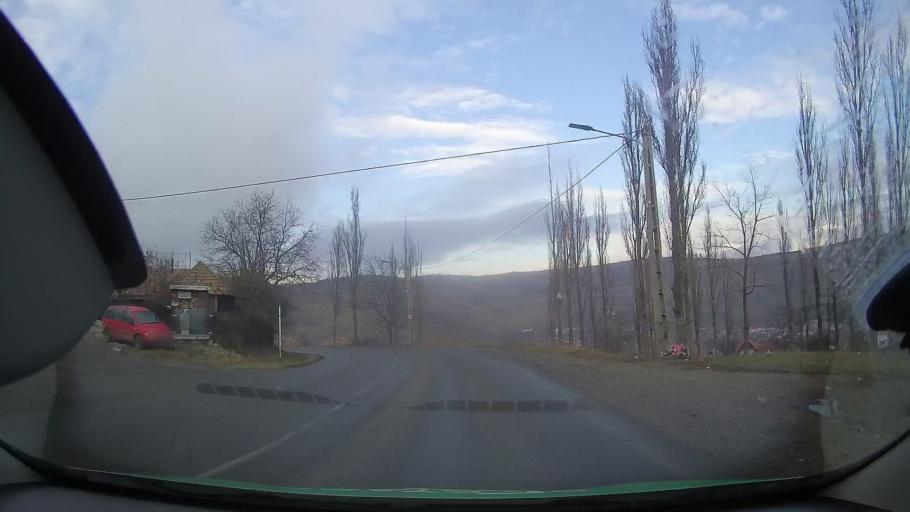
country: RO
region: Mures
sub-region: Municipiul Tarnaveni
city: Tarnaveni
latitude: 46.3373
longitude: 24.2798
